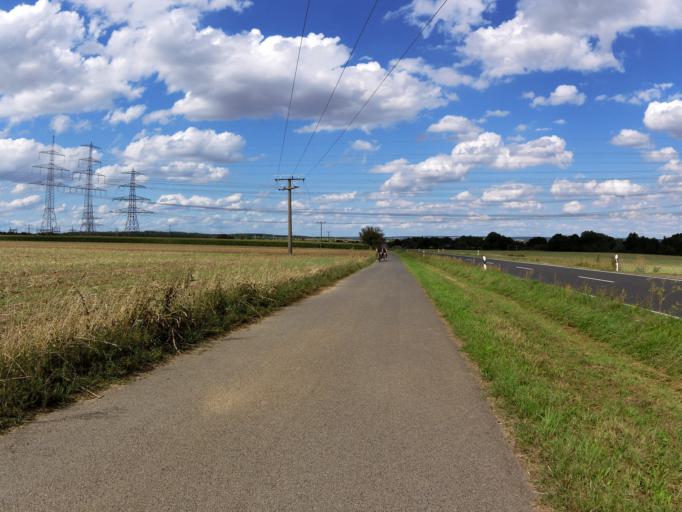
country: DE
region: Bavaria
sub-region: Regierungsbezirk Unterfranken
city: Bergrheinfeld
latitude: 49.9830
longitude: 10.1693
